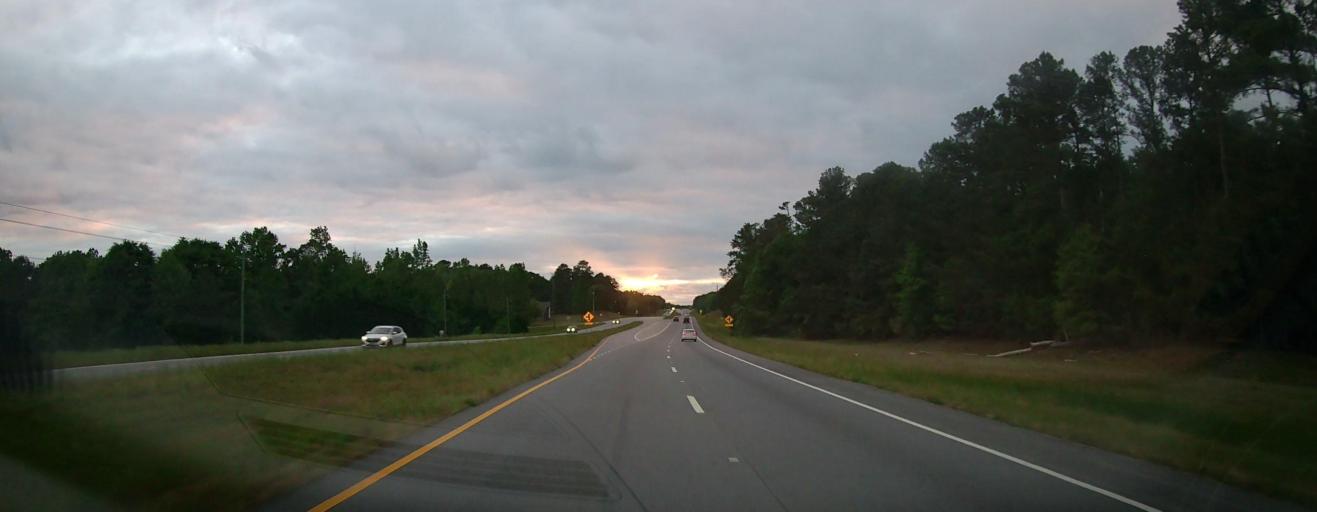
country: US
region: Georgia
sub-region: Clarke County
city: Country Club Estates
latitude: 34.0100
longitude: -83.4748
